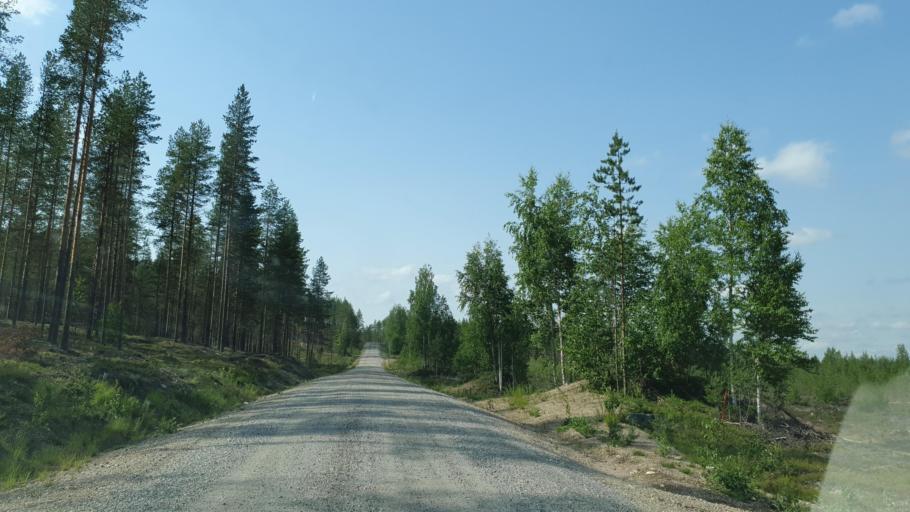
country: FI
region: Kainuu
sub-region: Kehys-Kainuu
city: Kuhmo
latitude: 64.0178
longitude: 29.9089
